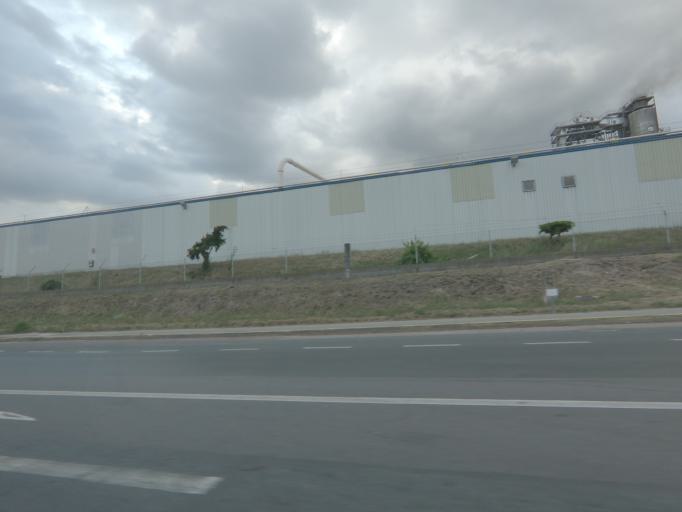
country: ES
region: Galicia
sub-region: Provincia de Ourense
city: Taboadela
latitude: 42.2887
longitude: -7.8239
